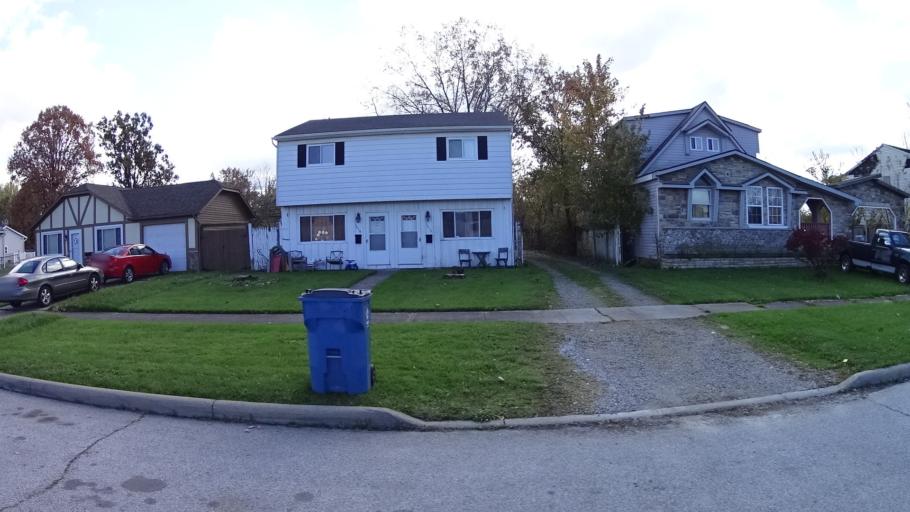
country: US
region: Ohio
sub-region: Lorain County
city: Lorain
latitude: 41.4409
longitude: -82.1453
